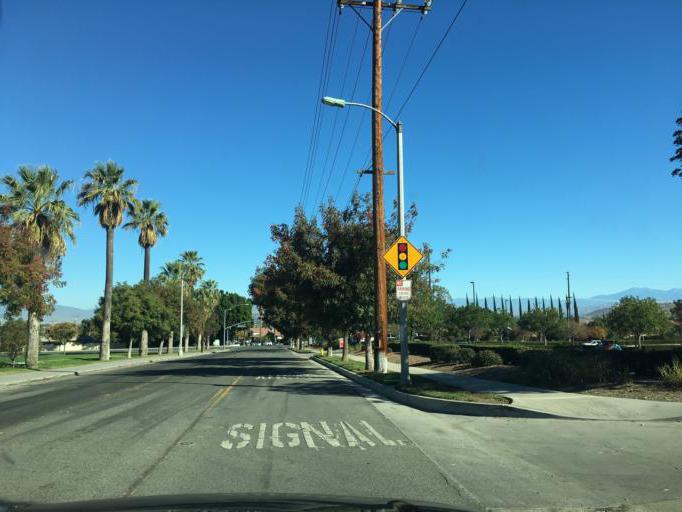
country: US
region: California
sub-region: Riverside County
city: Corona
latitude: 33.8526
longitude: -117.5571
